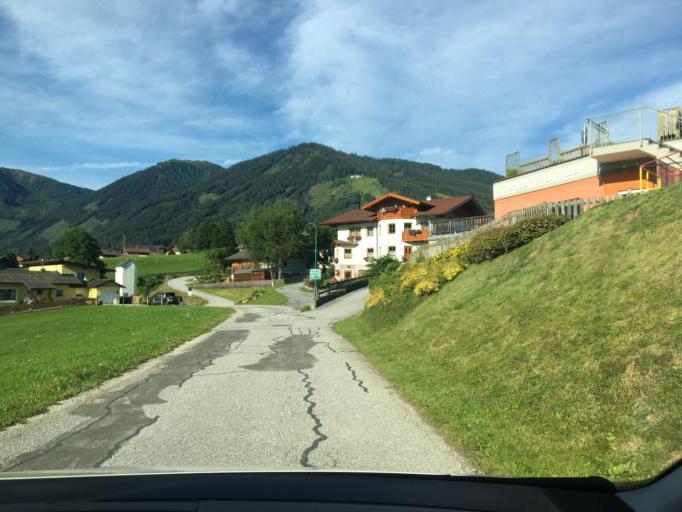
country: AT
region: Styria
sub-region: Politischer Bezirk Liezen
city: Schladming
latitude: 47.3806
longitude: 13.6720
